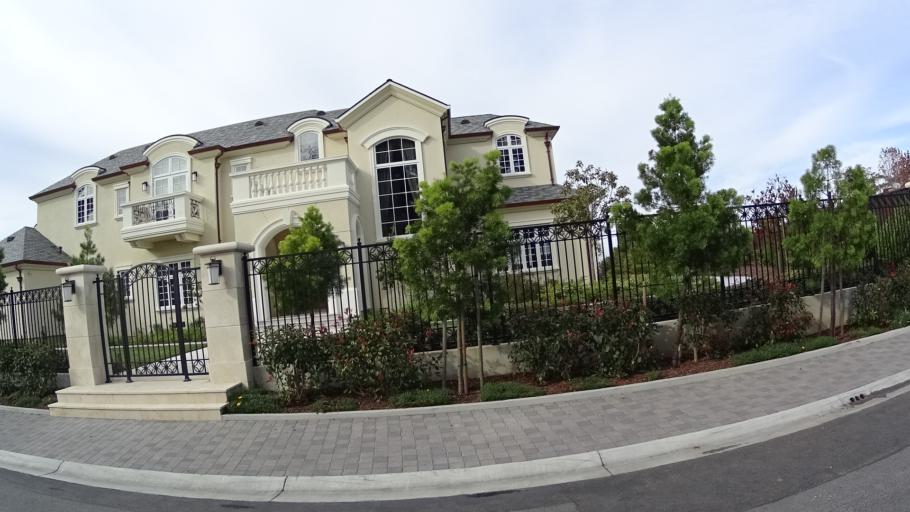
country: US
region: California
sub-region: San Mateo County
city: Hillsborough
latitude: 37.5727
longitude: -122.3835
